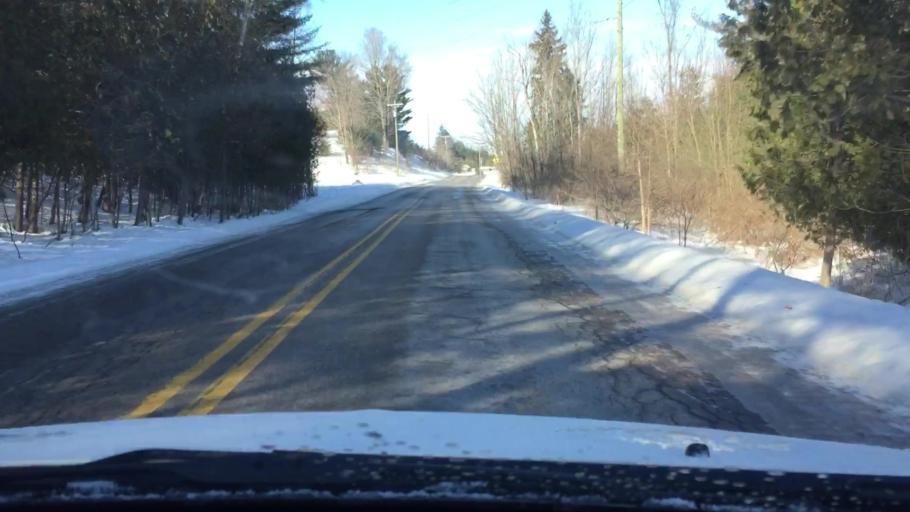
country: US
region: Michigan
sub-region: Charlevoix County
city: East Jordan
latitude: 45.1091
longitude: -85.1290
